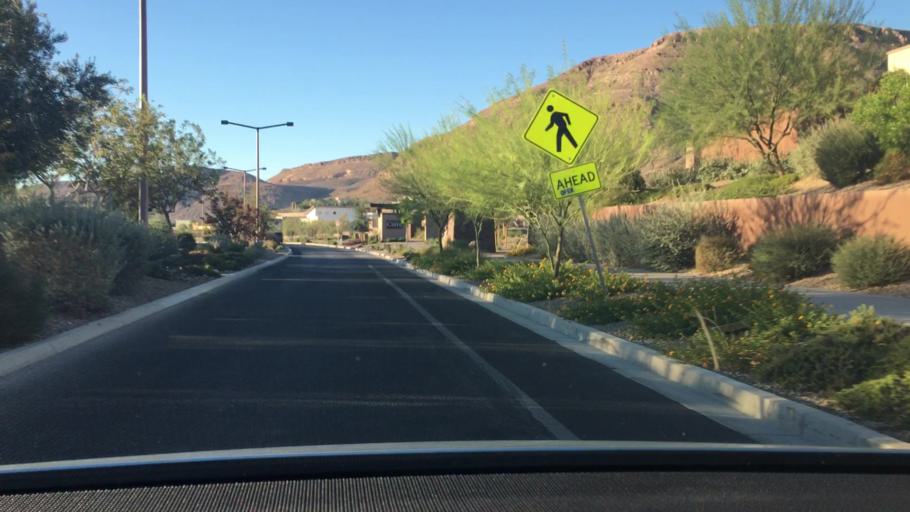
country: US
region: Nevada
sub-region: Clark County
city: Summerlin South
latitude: 36.0798
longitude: -115.3206
